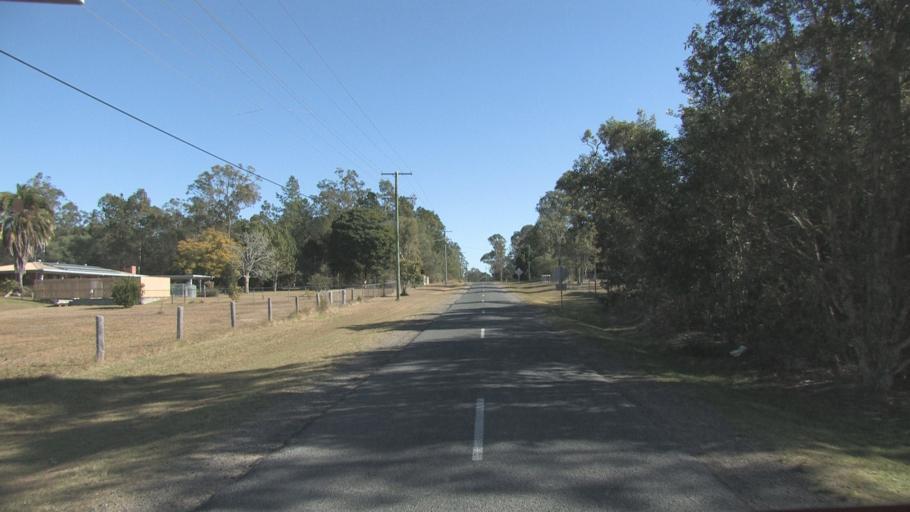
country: AU
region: Queensland
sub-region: Logan
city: North Maclean
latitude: -27.7901
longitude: 153.0468
